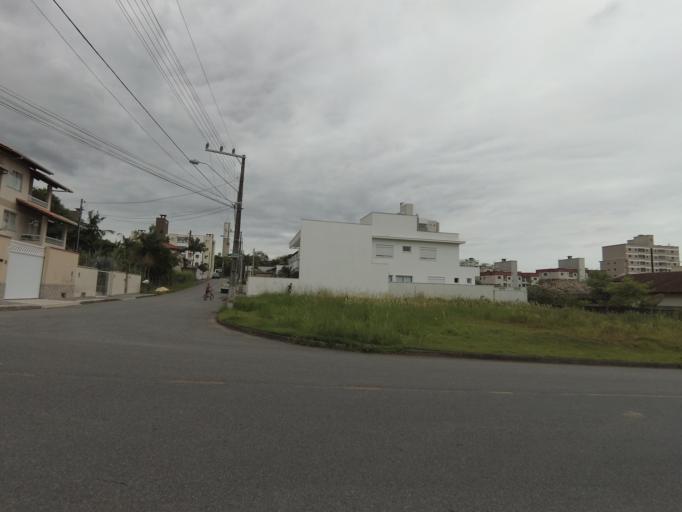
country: BR
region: Santa Catarina
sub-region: Blumenau
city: Blumenau
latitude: -26.9021
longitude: -49.1307
